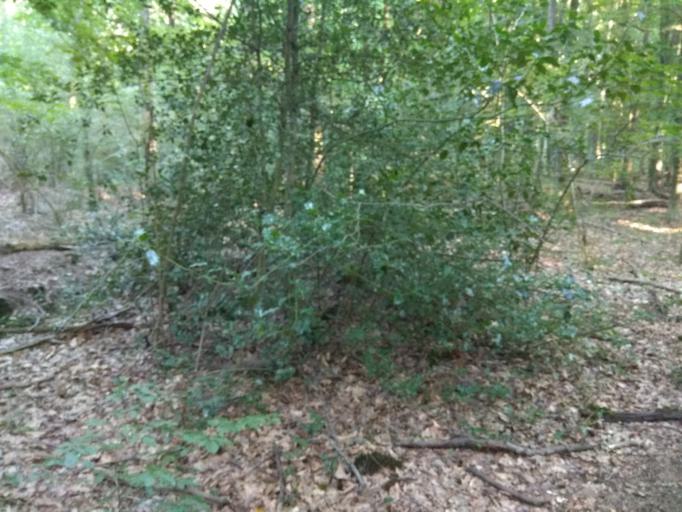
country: DE
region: North Rhine-Westphalia
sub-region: Regierungsbezirk Munster
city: Gladbeck
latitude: 51.6195
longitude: 6.9941
